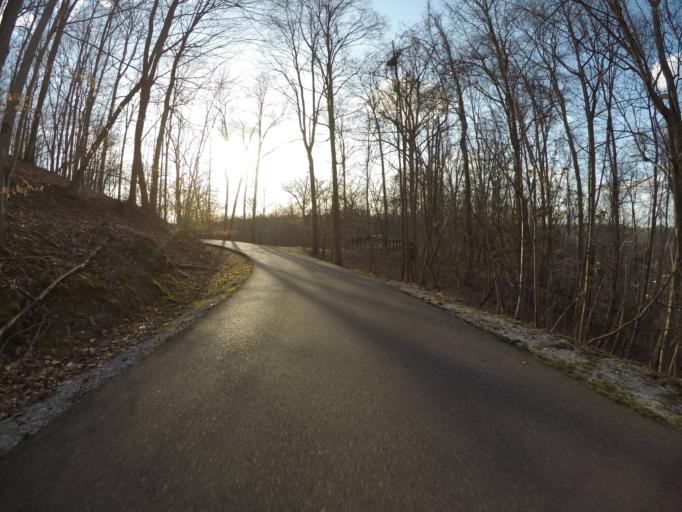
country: US
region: West Virginia
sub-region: Kanawha County
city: Charleston
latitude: 38.3914
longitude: -81.5680
